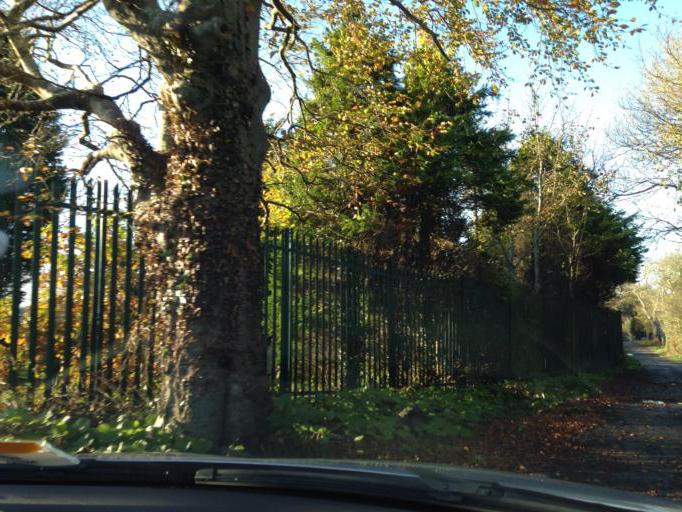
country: IE
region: Connaught
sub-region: County Galway
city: Gaillimh
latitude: 53.2785
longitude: -8.9845
